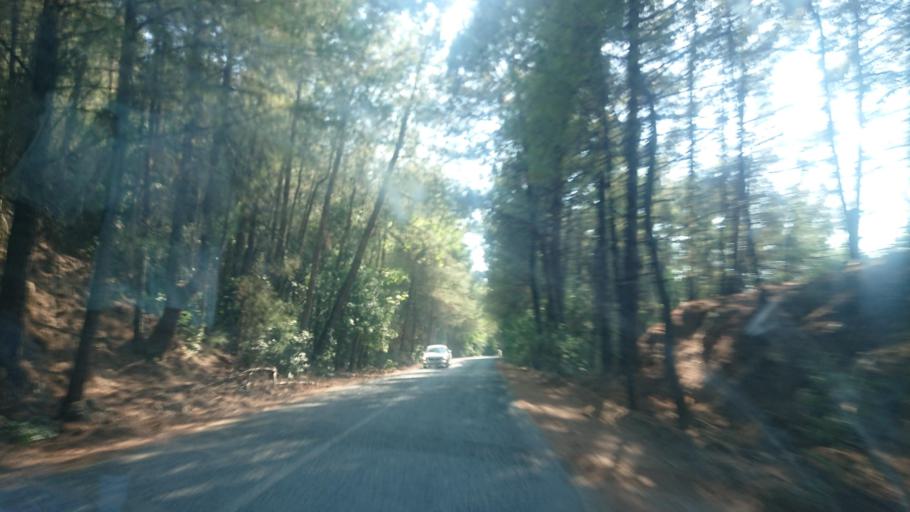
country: TR
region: Aydin
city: Atburgazi
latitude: 37.6913
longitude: 27.1495
